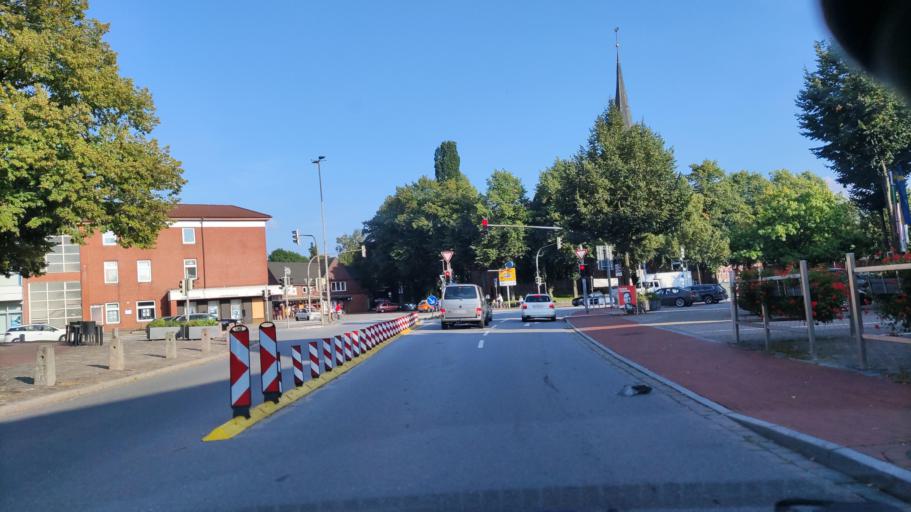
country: DE
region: Schleswig-Holstein
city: Bad Bramstedt
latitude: 53.9212
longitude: 9.8808
